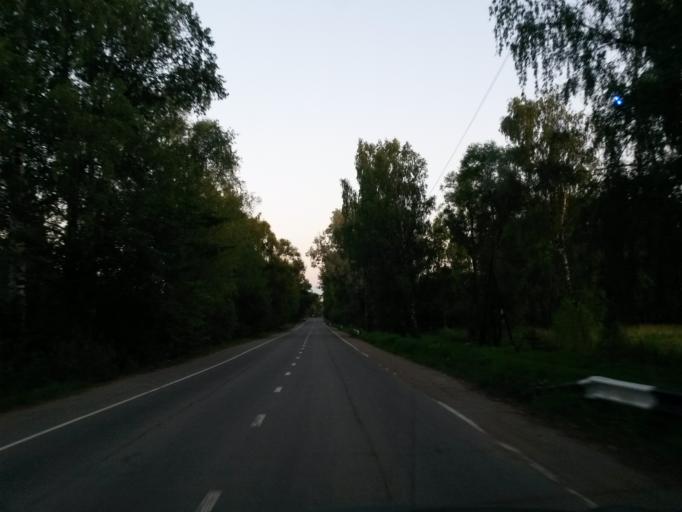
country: RU
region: Jaroslavl
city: Tutayev
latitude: 57.8958
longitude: 39.5277
